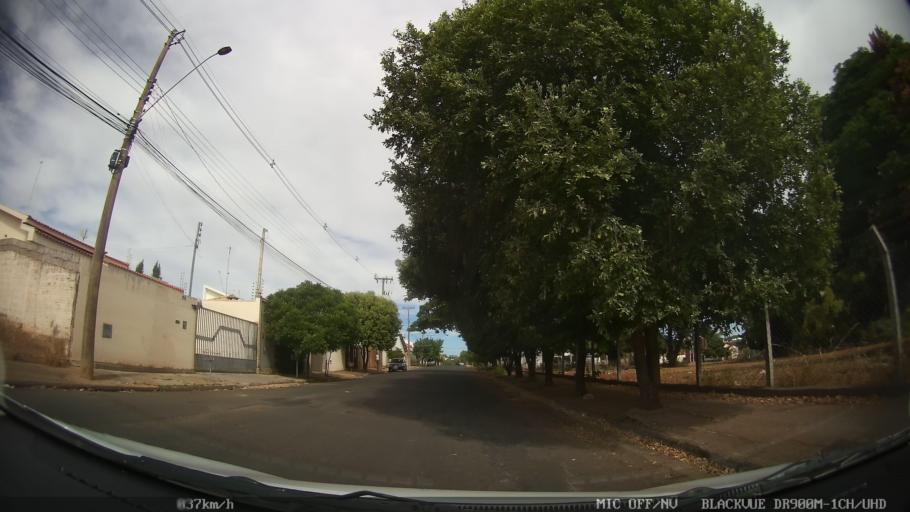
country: BR
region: Sao Paulo
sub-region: Catanduva
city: Catanduva
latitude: -21.1492
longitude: -48.9723
